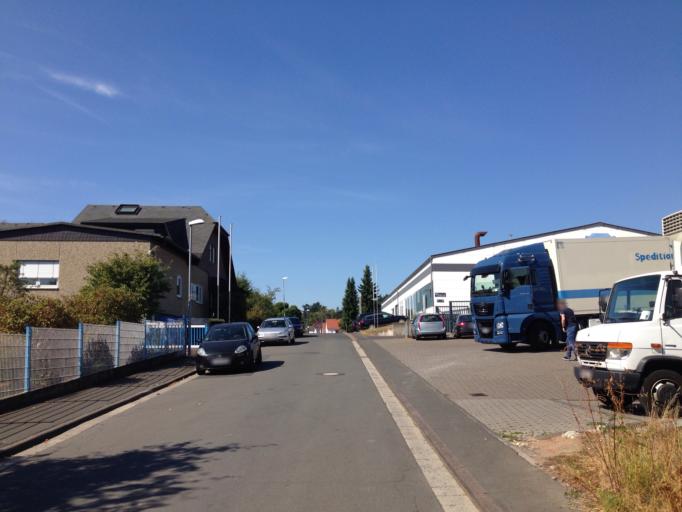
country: DE
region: Hesse
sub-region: Regierungsbezirk Giessen
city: Heuchelheim
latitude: 50.6134
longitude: 8.6117
